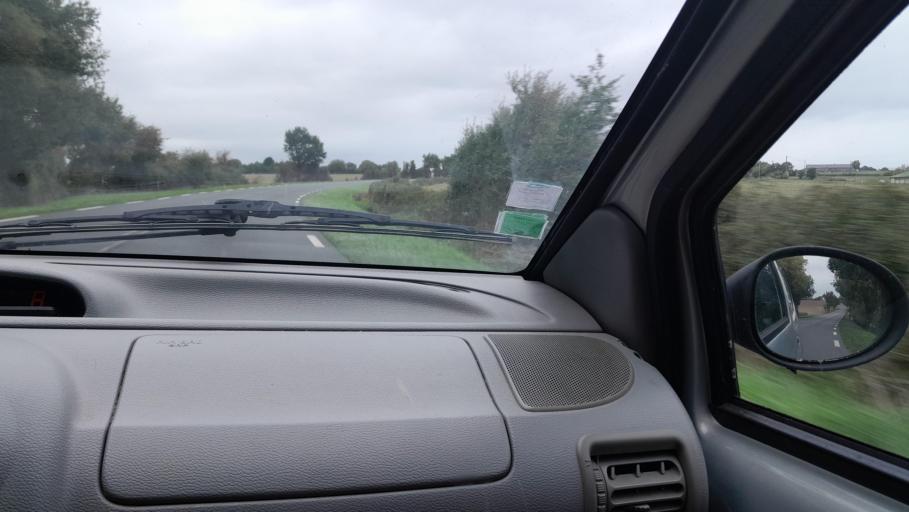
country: FR
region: Pays de la Loire
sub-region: Departement de la Loire-Atlantique
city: Saint-Mars-la-Jaille
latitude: 47.5878
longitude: -1.1961
